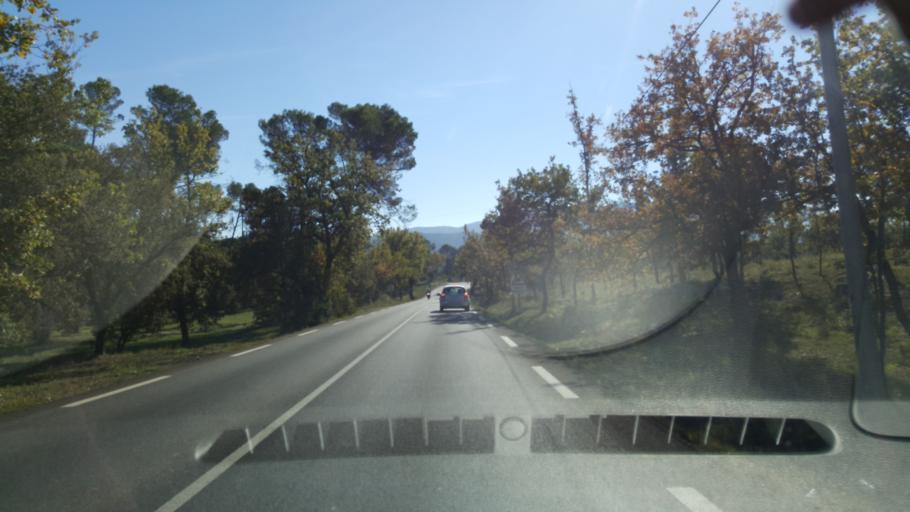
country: FR
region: Provence-Alpes-Cote d'Azur
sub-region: Departement du Var
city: Rougiers
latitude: 43.4109
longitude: 5.8252
